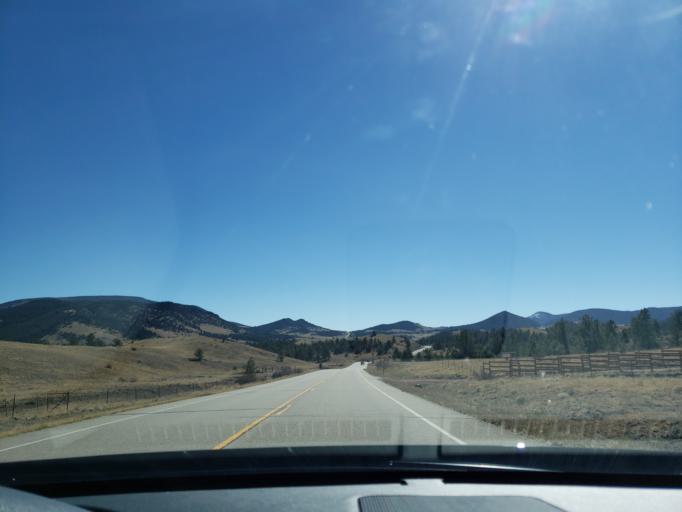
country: US
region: Colorado
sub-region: Chaffee County
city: Buena Vista
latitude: 38.8750
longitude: -105.6718
